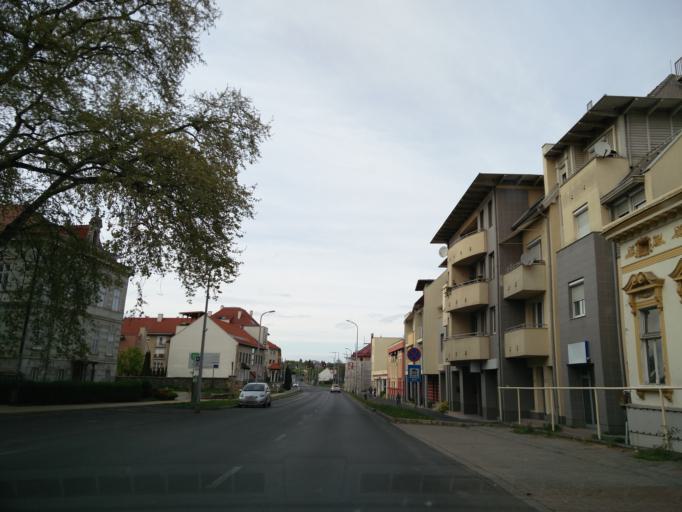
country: HU
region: Zala
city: Zalaegerszeg
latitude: 46.8461
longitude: 16.8468
